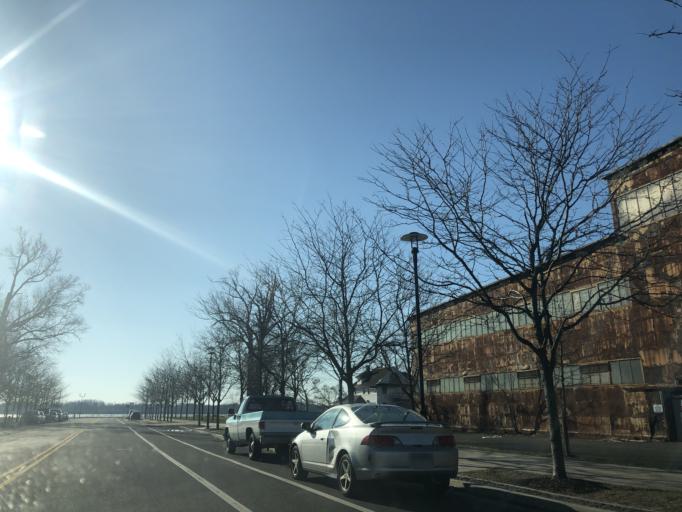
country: US
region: New Jersey
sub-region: Gloucester County
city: National Park
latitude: 39.8886
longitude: -75.1700
